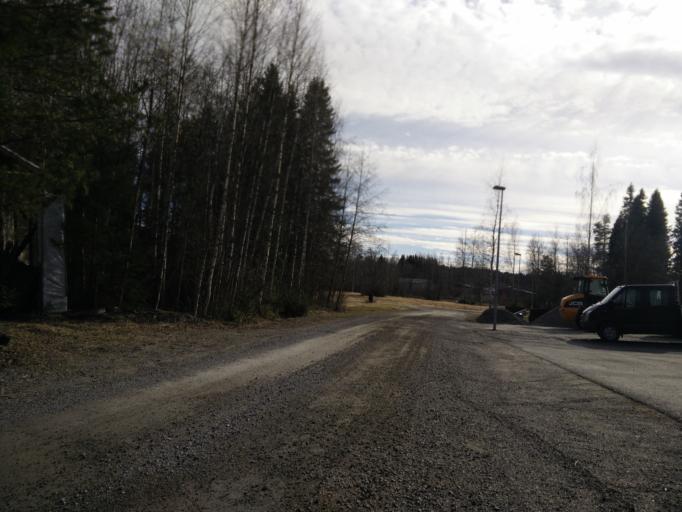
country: FI
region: Pirkanmaa
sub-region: Tampere
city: Orivesi
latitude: 61.6945
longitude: 24.3625
